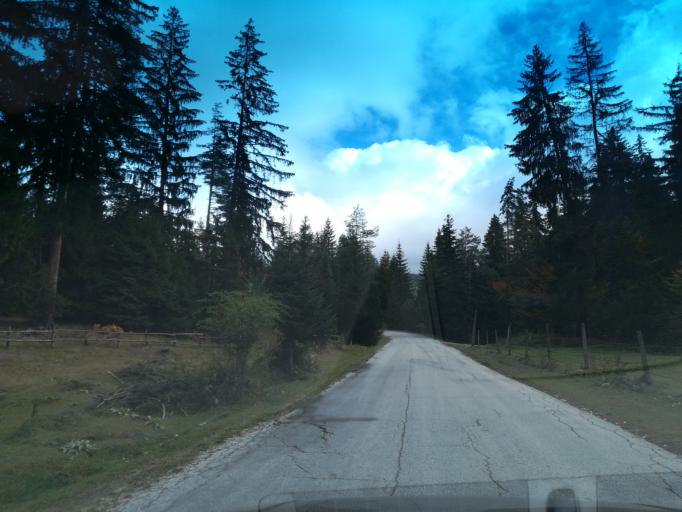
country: BG
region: Pazardzhik
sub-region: Obshtina Batak
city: Batak
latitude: 41.9268
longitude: 24.2757
